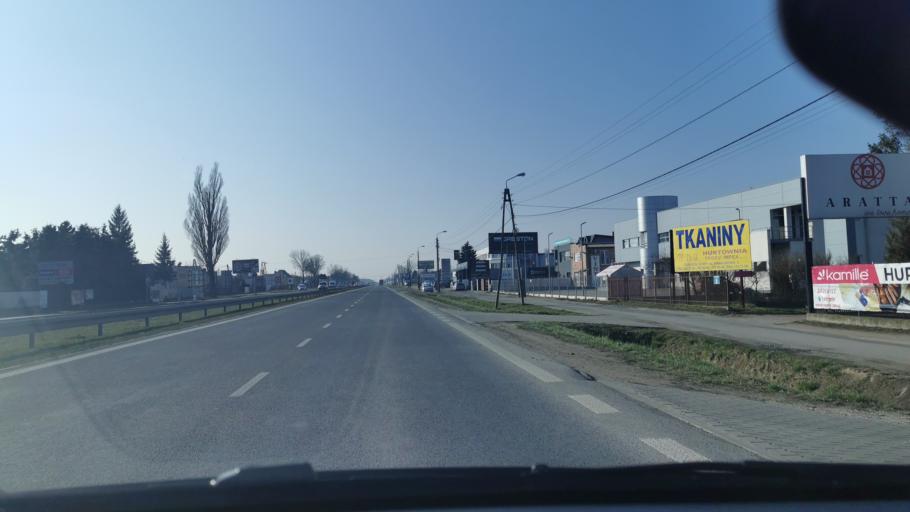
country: PL
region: Masovian Voivodeship
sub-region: Powiat pruszkowski
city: Nowe Grocholice
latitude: 52.1231
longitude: 20.8942
